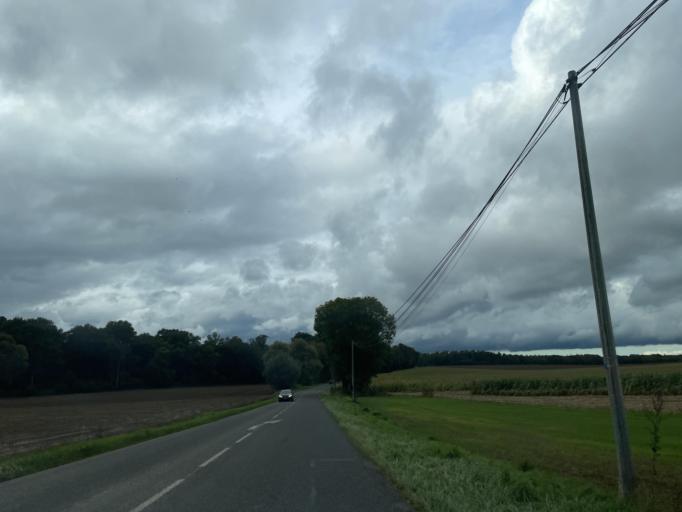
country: FR
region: Ile-de-France
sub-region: Departement de Seine-et-Marne
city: Saint-Jean-les-Deux-Jumeaux
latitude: 48.9064
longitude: 3.0259
